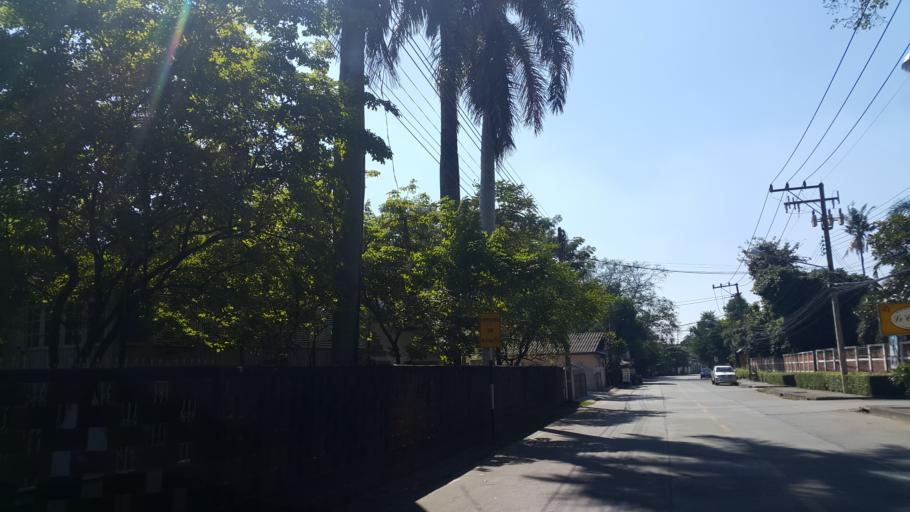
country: TH
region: Chiang Mai
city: Chiang Mai
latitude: 18.7605
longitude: 99.0036
